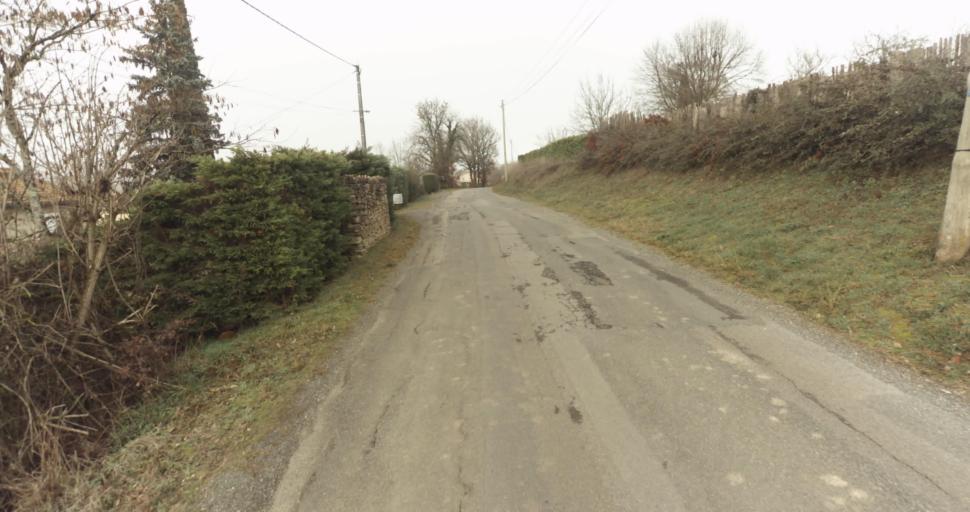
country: FR
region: Midi-Pyrenees
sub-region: Departement du Lot
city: Figeac
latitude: 44.6290
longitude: 2.0201
